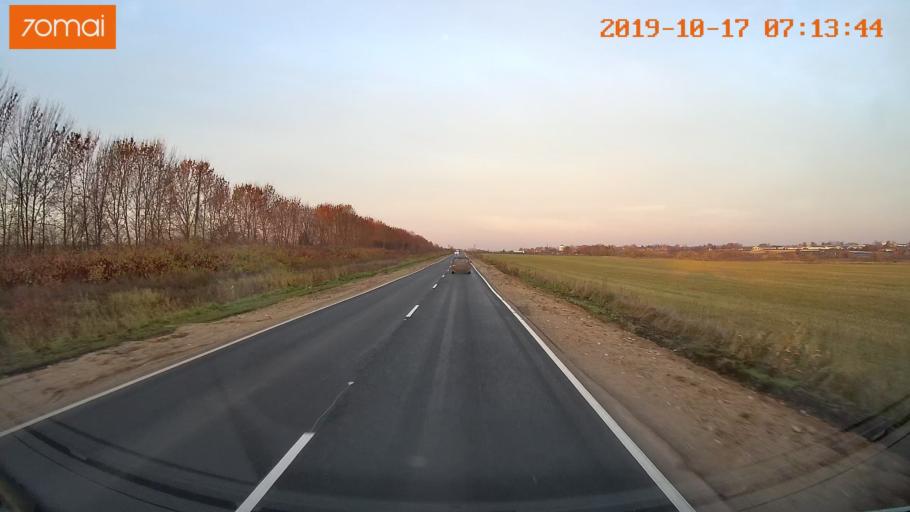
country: RU
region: Vladimir
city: Suzdal'
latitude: 56.3903
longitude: 40.3047
